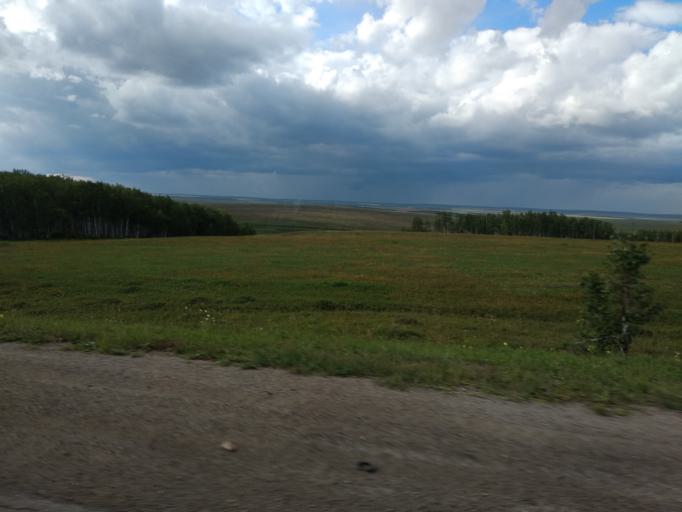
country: RU
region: Irkutsk
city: Bayanday
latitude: 53.0265
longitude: 105.4798
